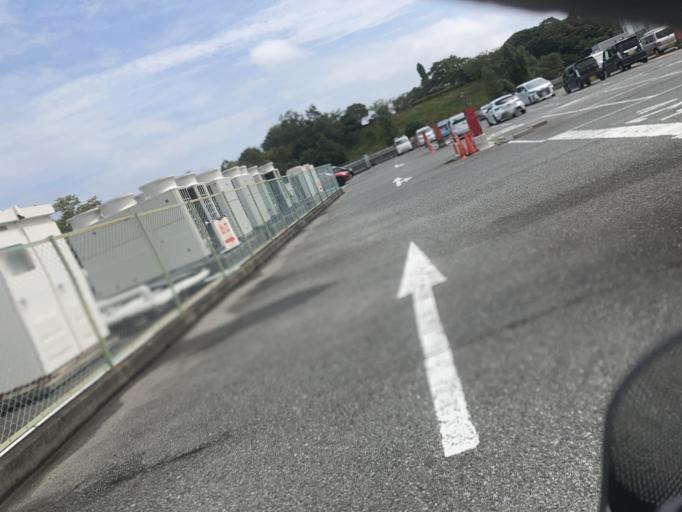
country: JP
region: Fukushima
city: Iwaki
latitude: 37.0133
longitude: 140.9167
